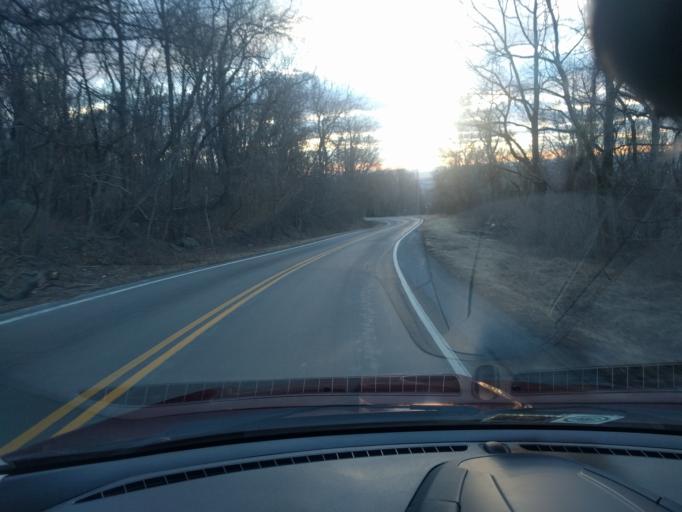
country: US
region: Virginia
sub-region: City of Bedford
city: Bedford
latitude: 37.4348
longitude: -79.5818
